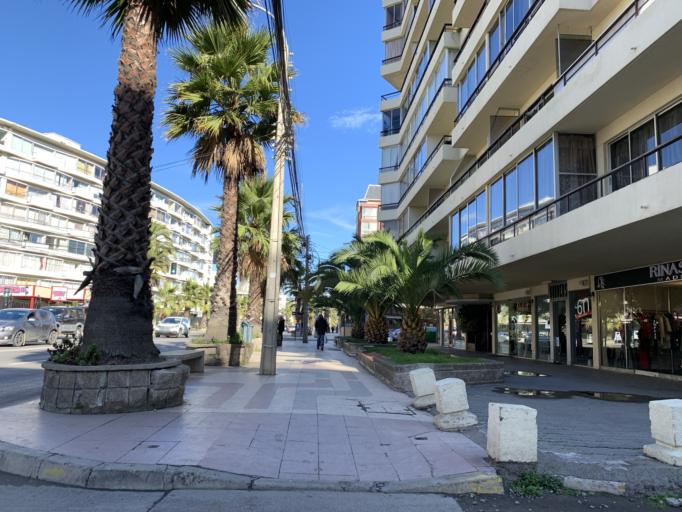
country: CL
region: Valparaiso
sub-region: Provincia de Valparaiso
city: Vina del Mar
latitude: -33.0152
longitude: -71.5559
